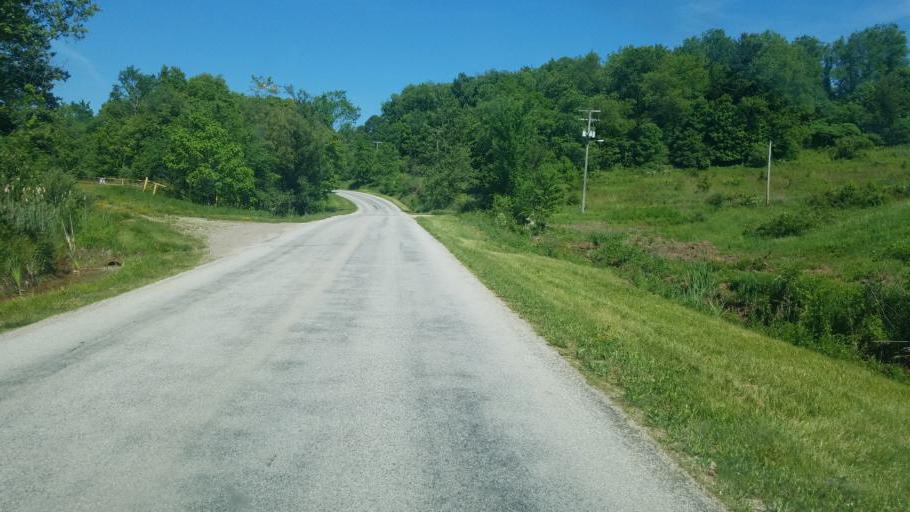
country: US
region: Ohio
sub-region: Coshocton County
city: Coshocton
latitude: 40.2275
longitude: -81.8259
